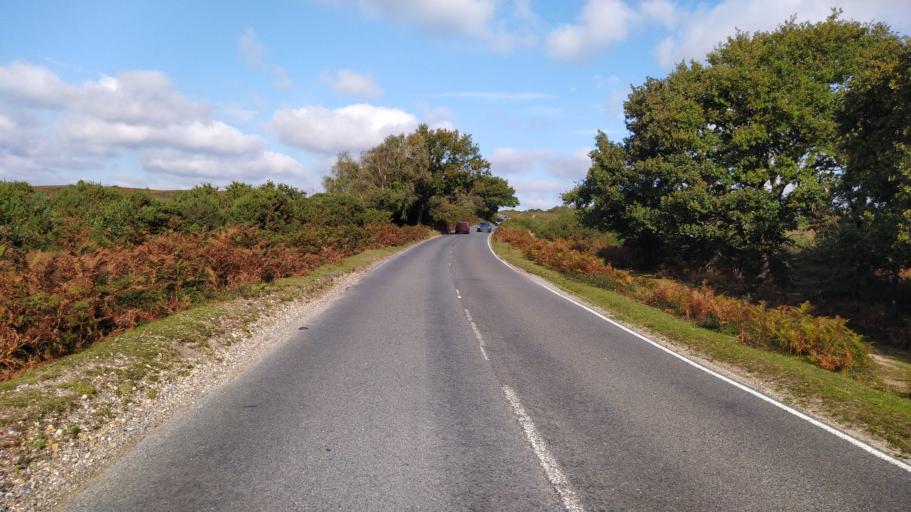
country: GB
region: England
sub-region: Hampshire
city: Bransgore
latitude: 50.8387
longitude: -1.7201
